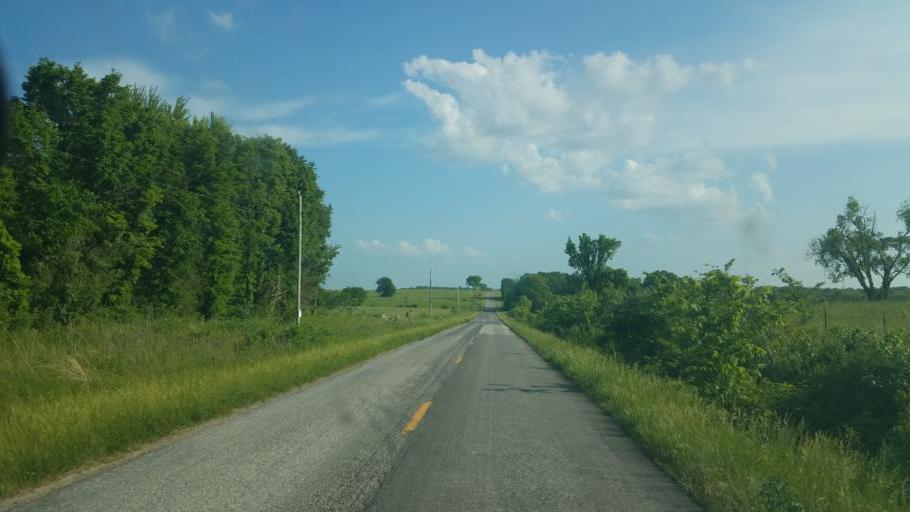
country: US
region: Missouri
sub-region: Moniteau County
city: California
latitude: 38.7790
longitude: -92.6051
